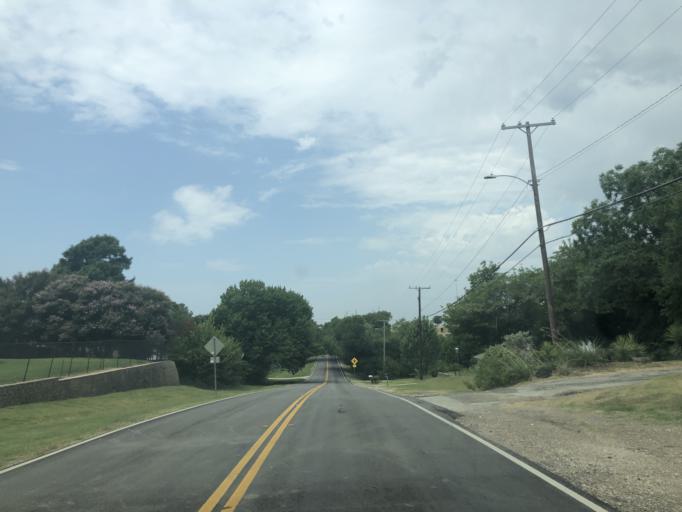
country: US
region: Texas
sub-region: Dallas County
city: Grand Prairie
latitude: 32.7643
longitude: -97.0240
